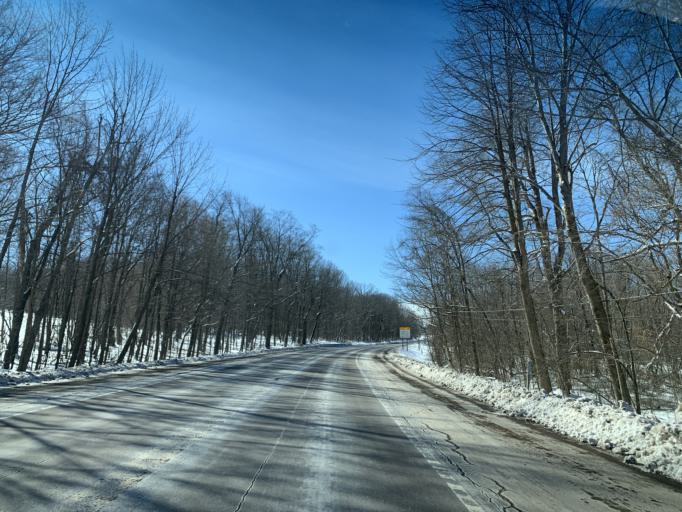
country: US
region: Pennsylvania
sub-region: Somerset County
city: Meyersdale
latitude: 39.7204
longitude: -79.0880
